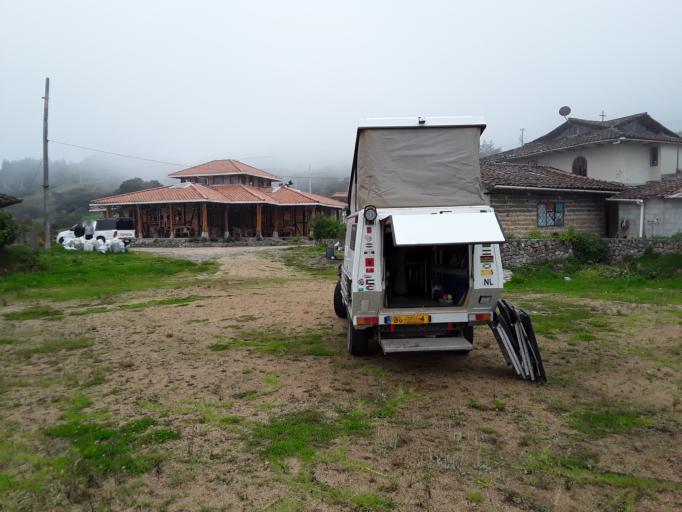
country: EC
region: Loja
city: Loja
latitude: -3.6481
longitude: -79.2547
